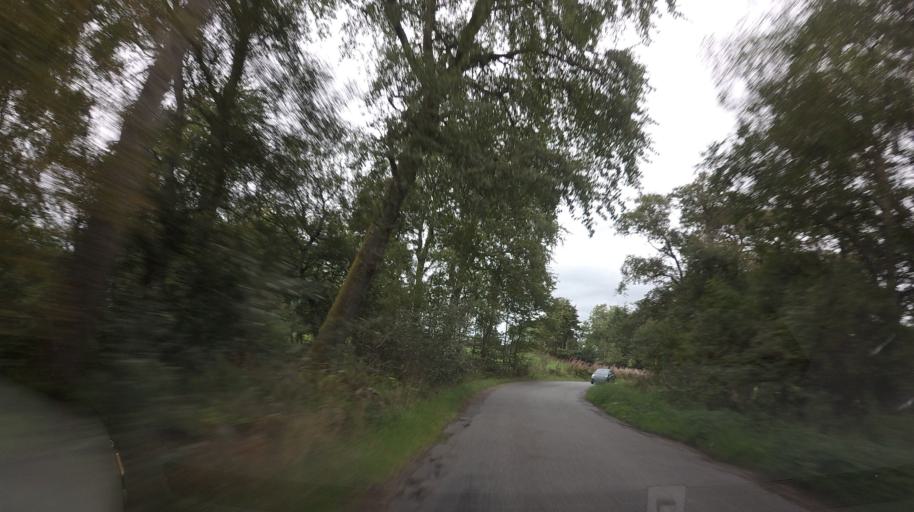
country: GB
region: Scotland
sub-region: Aberdeenshire
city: Banchory
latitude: 57.0861
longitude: -2.4508
